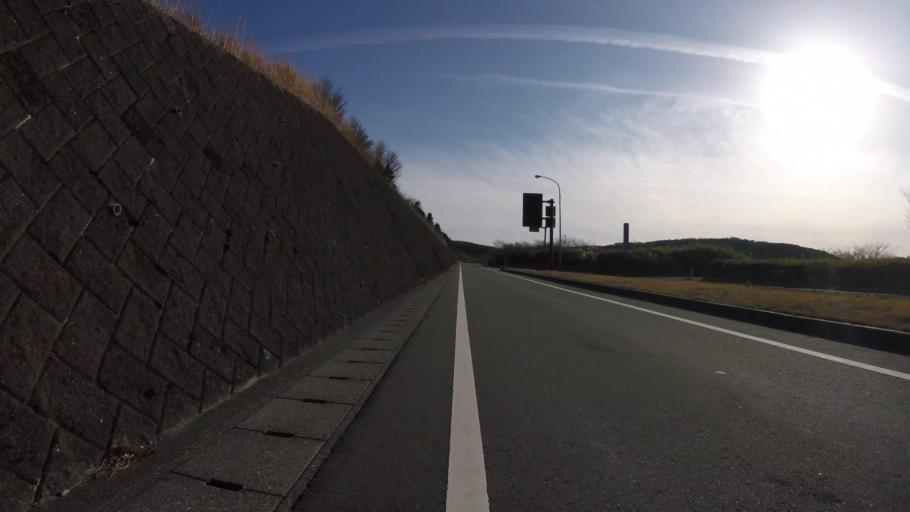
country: JP
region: Kanagawa
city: Hakone
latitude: 35.1665
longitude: 139.0289
